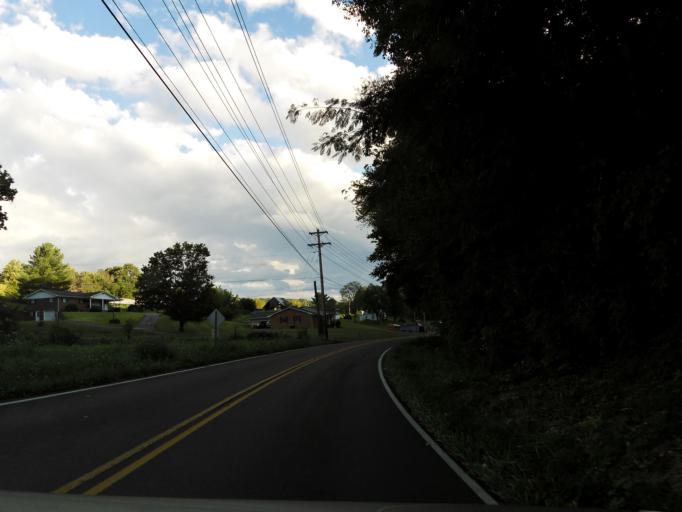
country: US
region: Tennessee
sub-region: Grainger County
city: Rutledge
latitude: 36.2541
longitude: -83.5255
